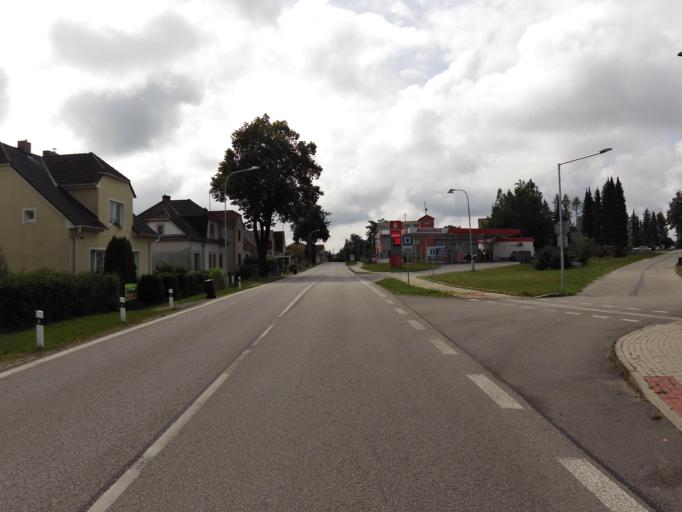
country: CZ
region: Jihocesky
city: Suchdol nad Luznici
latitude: 48.8977
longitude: 14.8813
